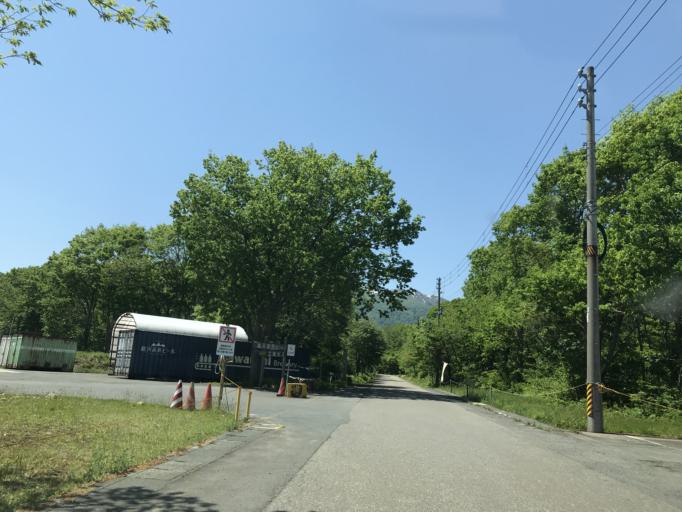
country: JP
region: Iwate
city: Shizukuishi
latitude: 39.5436
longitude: 140.8269
